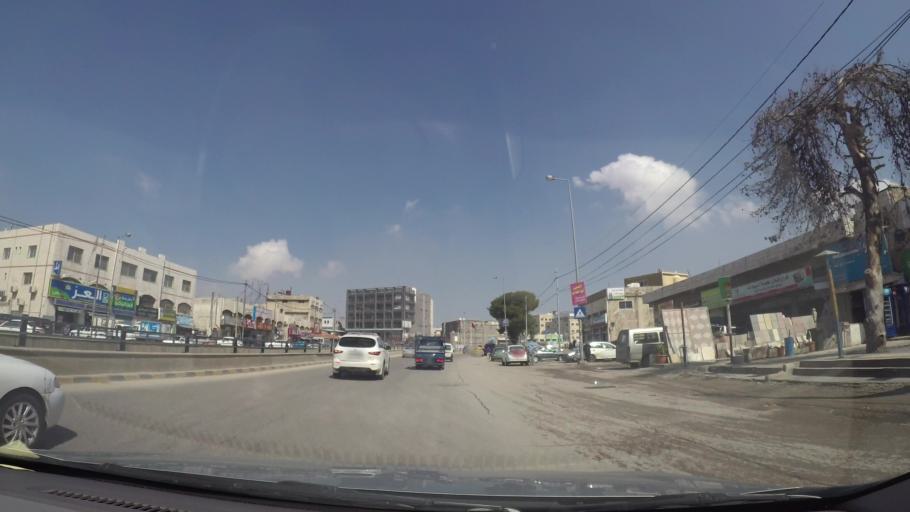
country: JO
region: Amman
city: Al Bunayyat ash Shamaliyah
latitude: 31.9157
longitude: 35.9027
